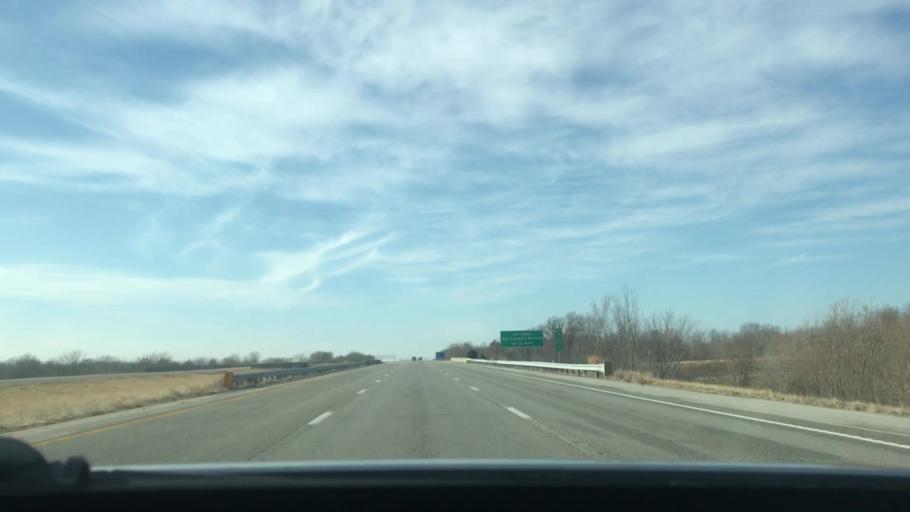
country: US
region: Missouri
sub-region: Platte County
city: Weatherby Lake
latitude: 39.3077
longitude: -94.6470
